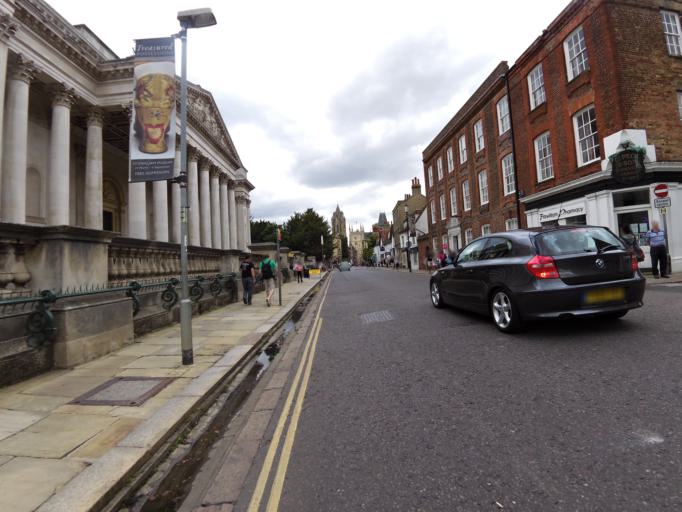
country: GB
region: England
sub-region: Cambridgeshire
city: Cambridge
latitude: 52.2001
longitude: 0.1202
